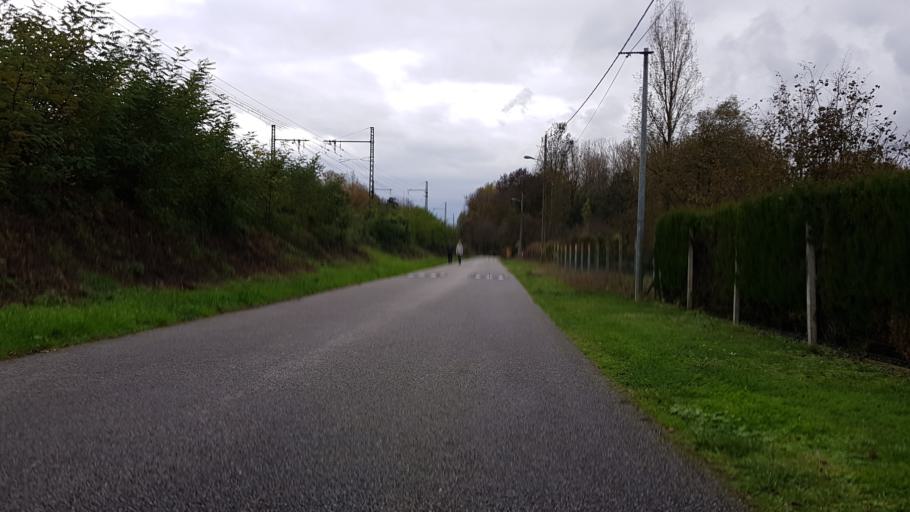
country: FR
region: Poitou-Charentes
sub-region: Departement de la Vienne
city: Chasseneuil-du-Poitou
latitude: 46.6386
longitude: 0.3626
